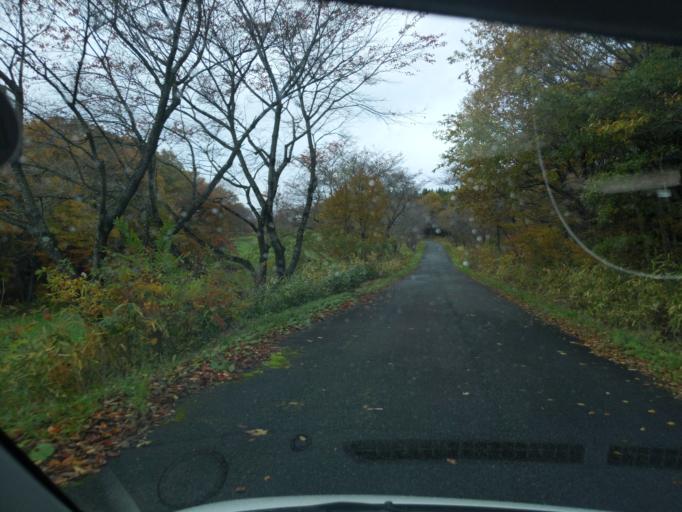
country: JP
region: Iwate
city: Mizusawa
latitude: 39.0684
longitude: 141.0404
